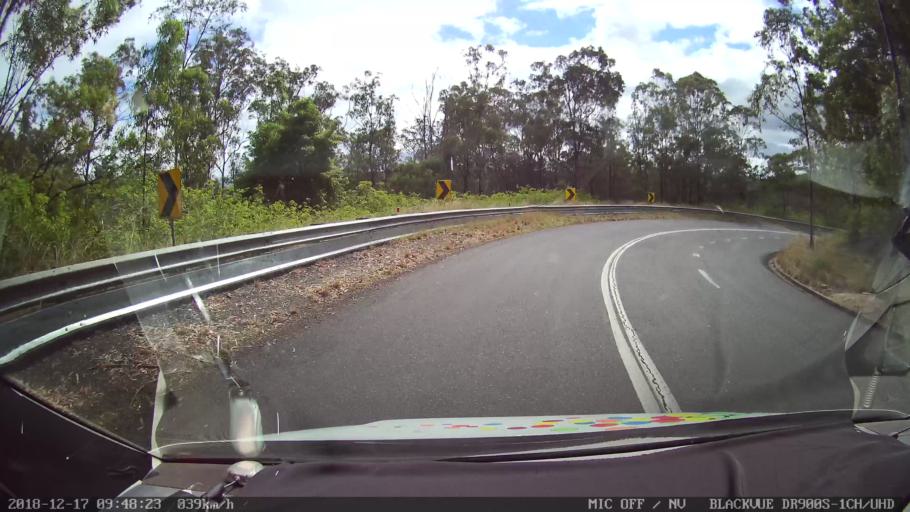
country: AU
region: New South Wales
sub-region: Tenterfield Municipality
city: Carrolls Creek
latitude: -28.9239
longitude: 152.3439
